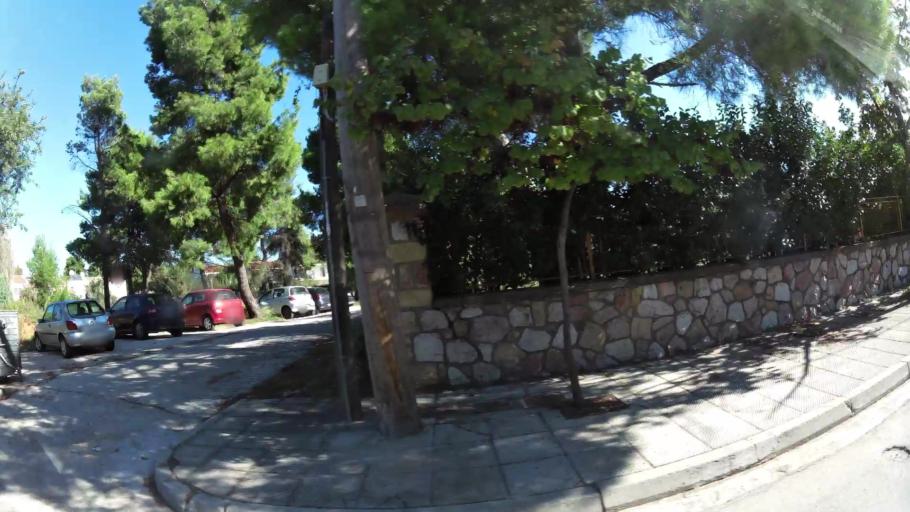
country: GR
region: Attica
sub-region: Nomarchia Anatolikis Attikis
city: Drosia
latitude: 38.1215
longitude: 23.8706
